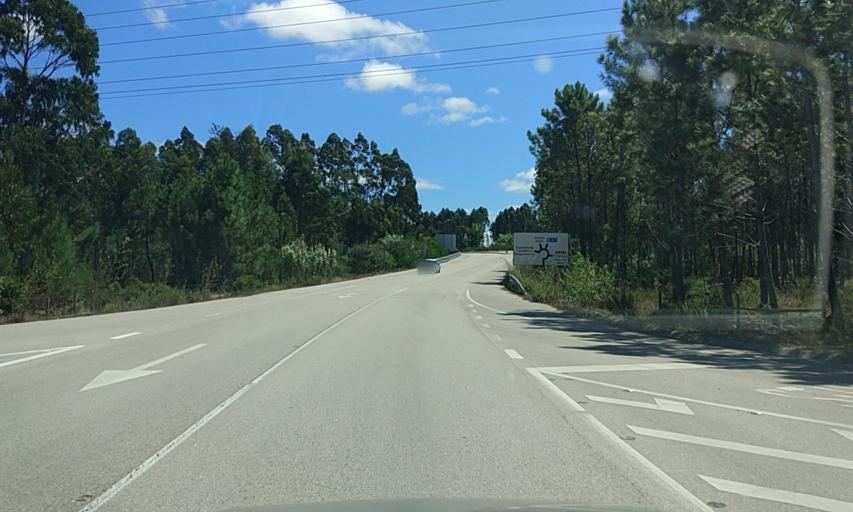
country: PT
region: Coimbra
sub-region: Montemor-O-Velho
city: Arazede
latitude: 40.3334
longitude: -8.7288
